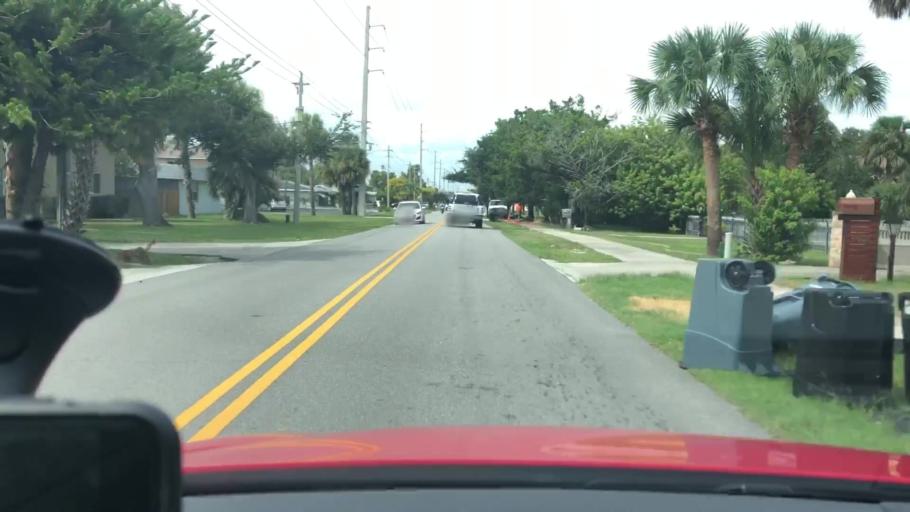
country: US
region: Florida
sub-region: Volusia County
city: South Daytona
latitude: 29.1765
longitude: -81.0026
